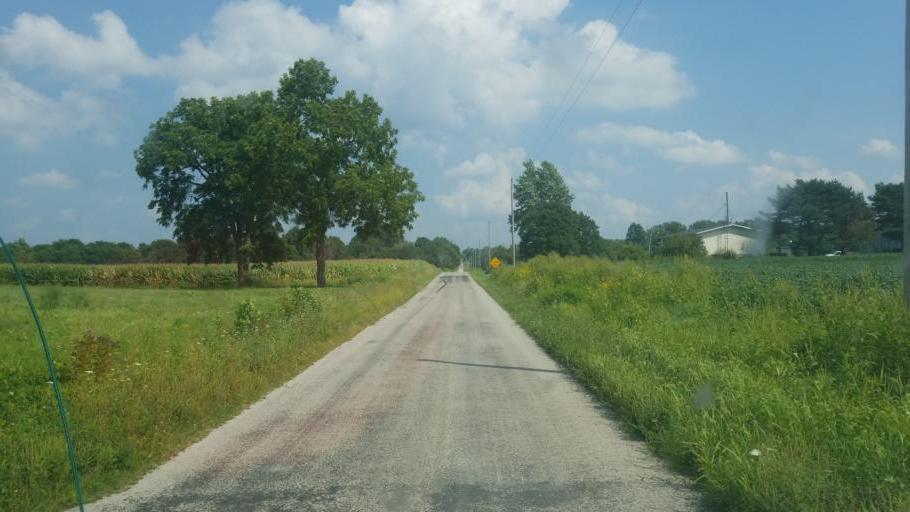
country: US
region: Ohio
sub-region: Huron County
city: New London
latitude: 41.0490
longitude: -82.4258
